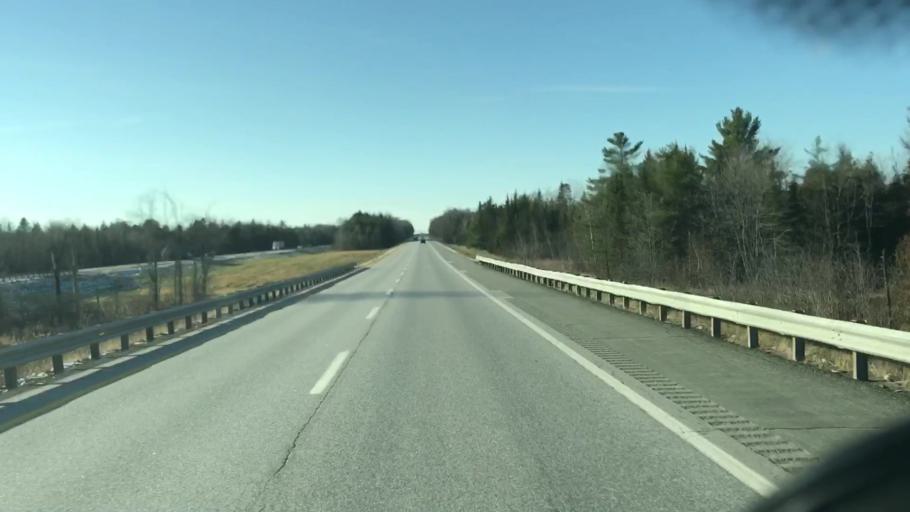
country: US
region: Maine
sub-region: Penobscot County
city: Carmel
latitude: 44.7759
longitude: -69.0428
